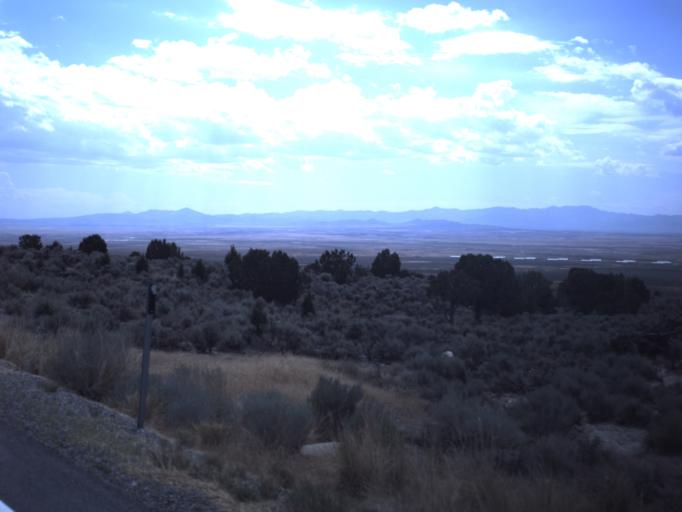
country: US
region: Utah
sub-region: Tooele County
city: Tooele
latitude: 40.3157
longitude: -112.2839
